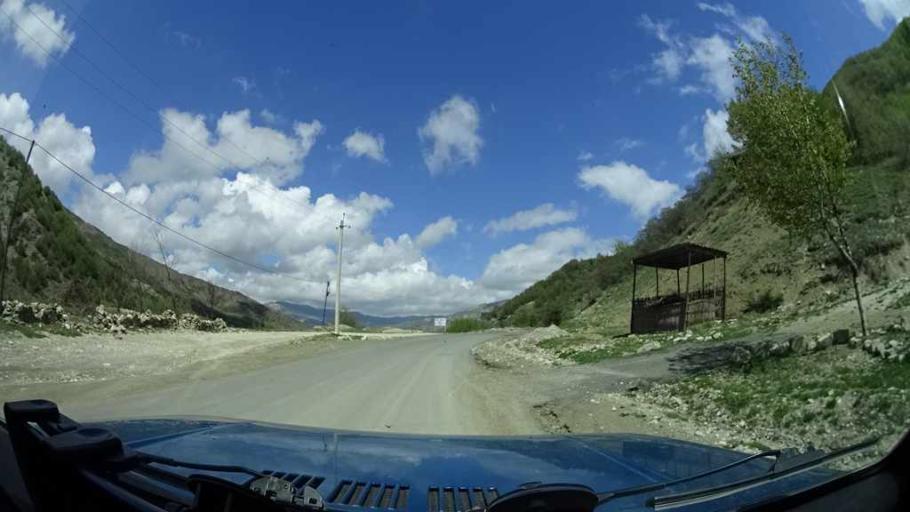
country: AZ
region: Ismayilli
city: Basqal
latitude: 40.8406
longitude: 48.3673
